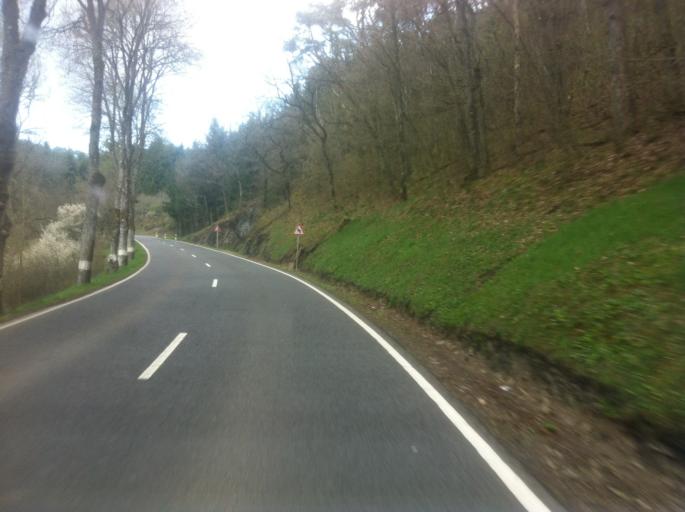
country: LU
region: Diekirch
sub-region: Canton de Wiltz
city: Eschweiler
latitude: 49.9802
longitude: 5.9611
